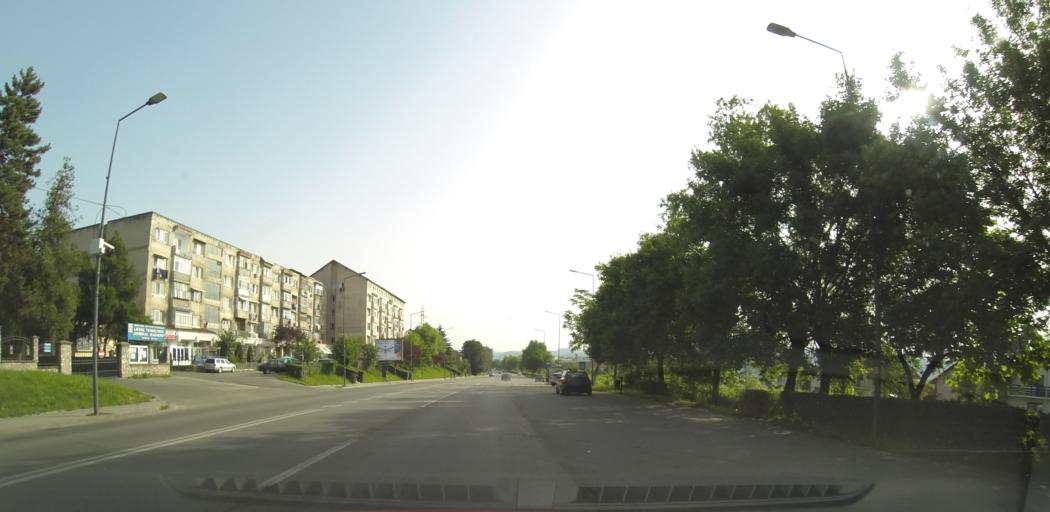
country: RO
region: Valcea
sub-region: Municipiul Ramnicu Valcea
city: Ramnicu Valcea
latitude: 45.0848
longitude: 24.3570
